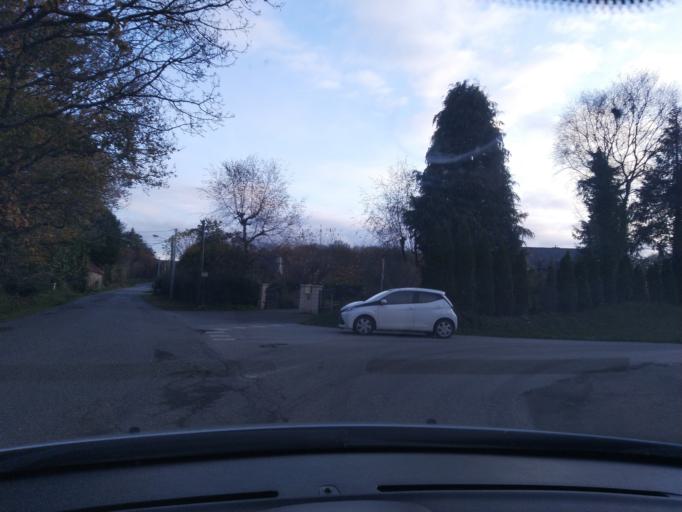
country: FR
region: Brittany
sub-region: Departement du Finistere
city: Plouigneau
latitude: 48.5754
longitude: -3.7082
